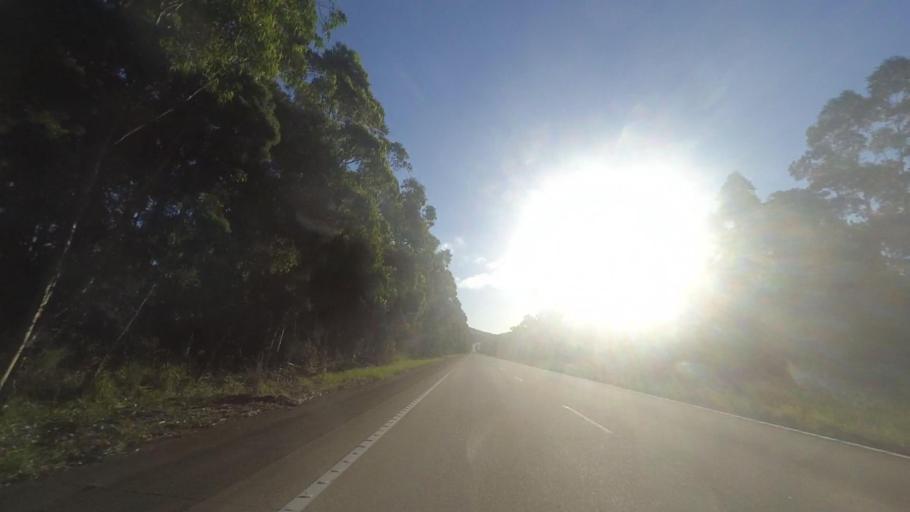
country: AU
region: New South Wales
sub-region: Great Lakes
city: Bulahdelah
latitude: -32.3775
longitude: 152.2738
